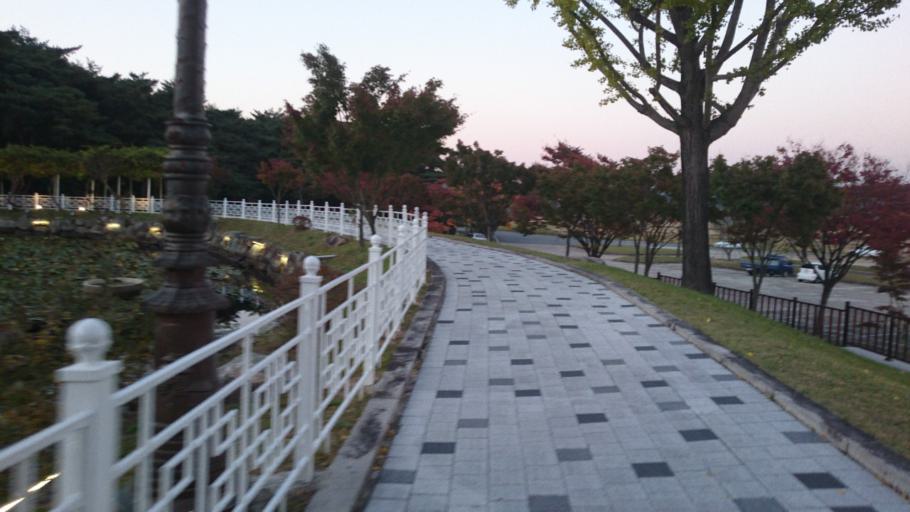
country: KR
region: Gyeongsangbuk-do
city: Kyonju
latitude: 35.7987
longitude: 129.2421
